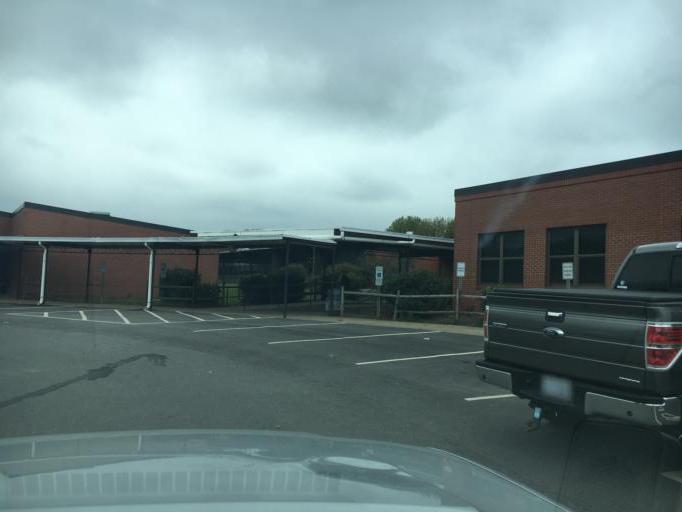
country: US
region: North Carolina
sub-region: Buncombe County
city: Woodfin
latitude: 35.6176
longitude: -82.6292
